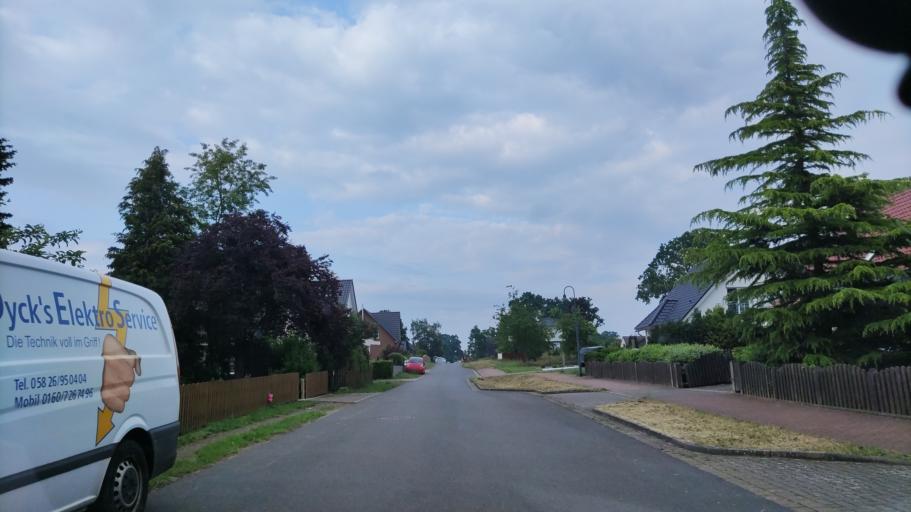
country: DE
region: Lower Saxony
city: Suderburg
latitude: 52.8942
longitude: 10.4384
